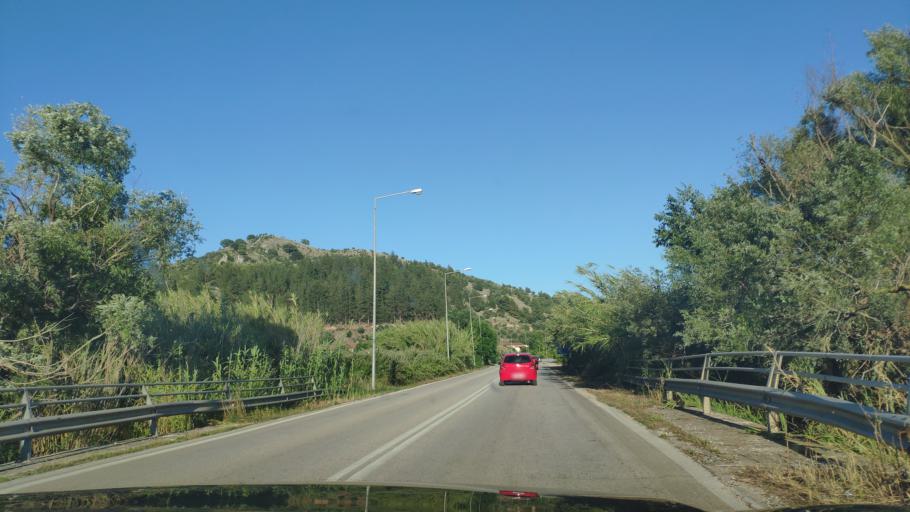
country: GR
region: Epirus
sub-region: Nomos Prevezis
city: Louros
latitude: 39.1784
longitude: 20.7859
